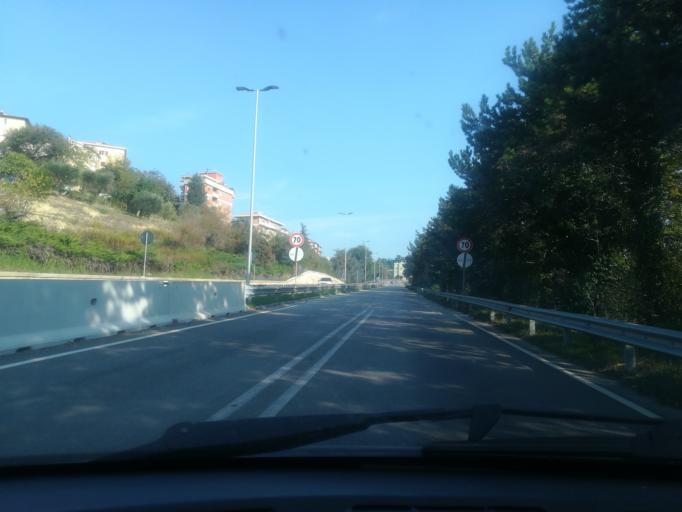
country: IT
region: The Marches
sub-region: Provincia di Macerata
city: Macerata
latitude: 43.2919
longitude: 13.4505
